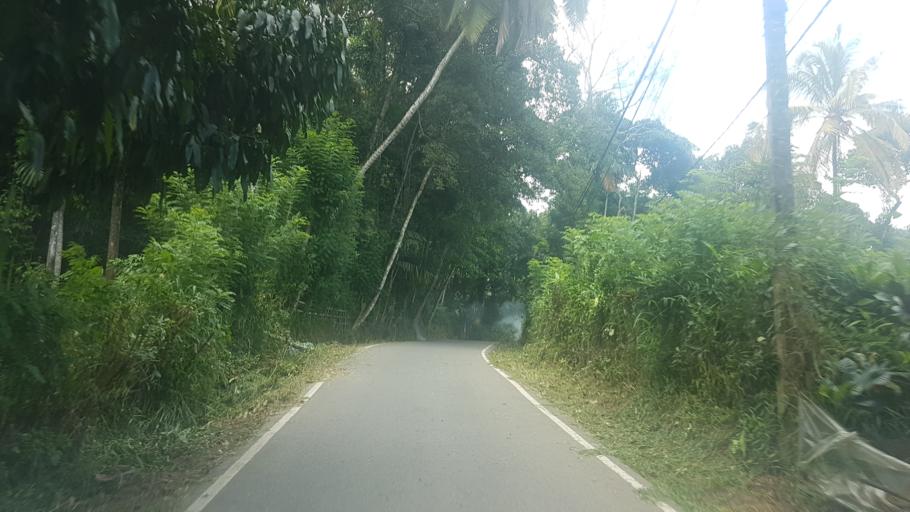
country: LK
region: Central
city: Gampola
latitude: 7.2174
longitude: 80.5879
